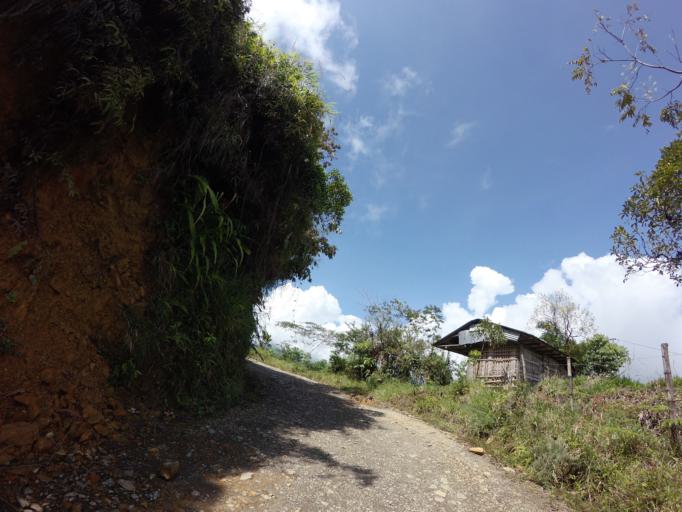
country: CO
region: Antioquia
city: Narino
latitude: 5.5148
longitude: -75.1698
